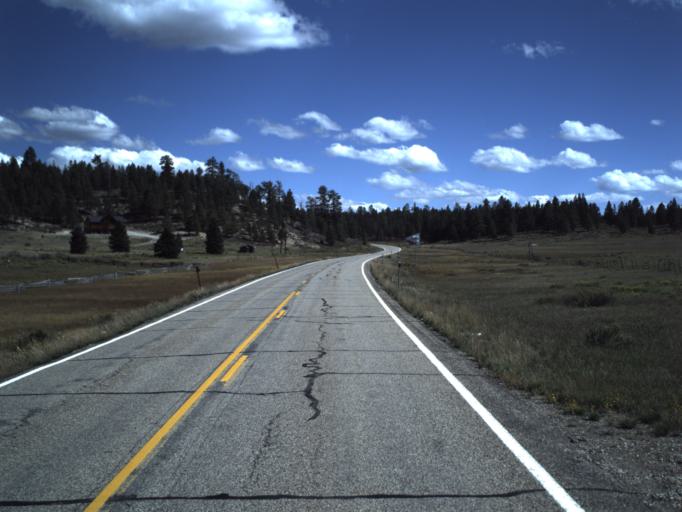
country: US
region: Utah
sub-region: Garfield County
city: Panguitch
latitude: 37.4940
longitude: -112.5763
